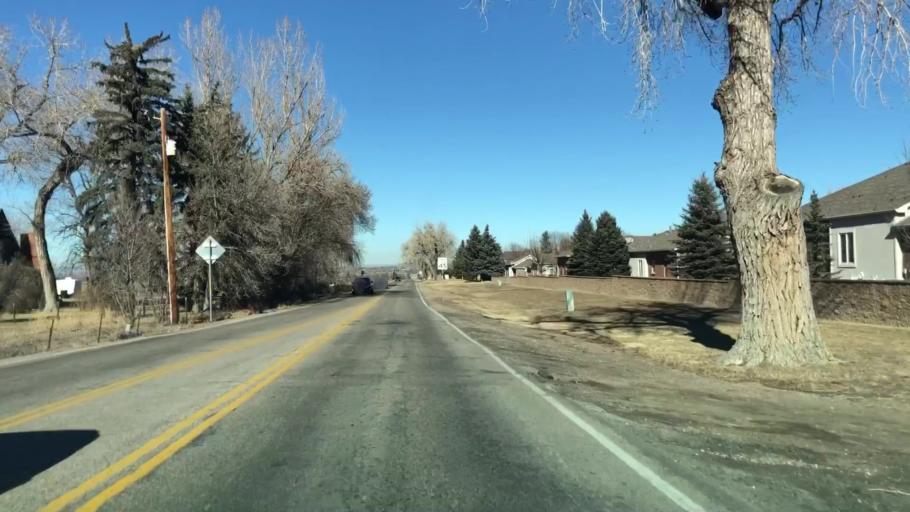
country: US
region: Colorado
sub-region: Weld County
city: Windsor
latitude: 40.4802
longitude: -104.9820
